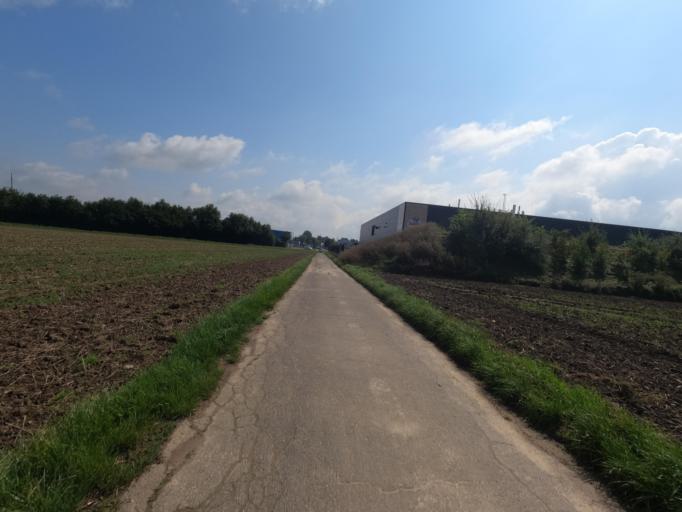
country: DE
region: North Rhine-Westphalia
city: Baesweiler
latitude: 50.9195
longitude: 6.1693
